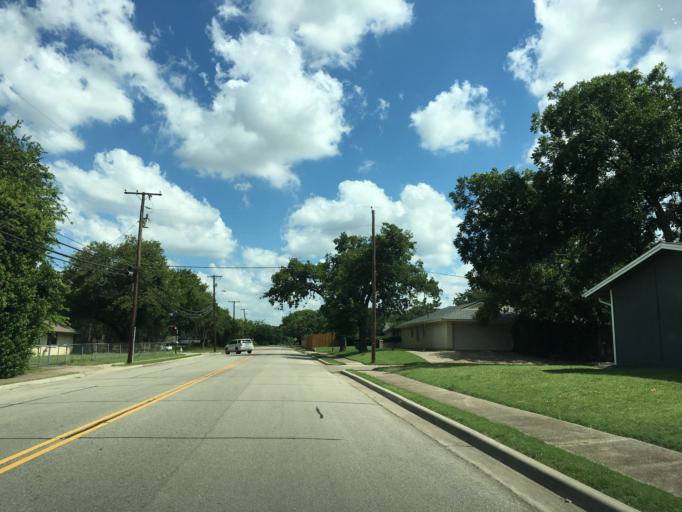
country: US
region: Texas
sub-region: Dallas County
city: Farmers Branch
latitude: 32.9211
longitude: -96.8647
